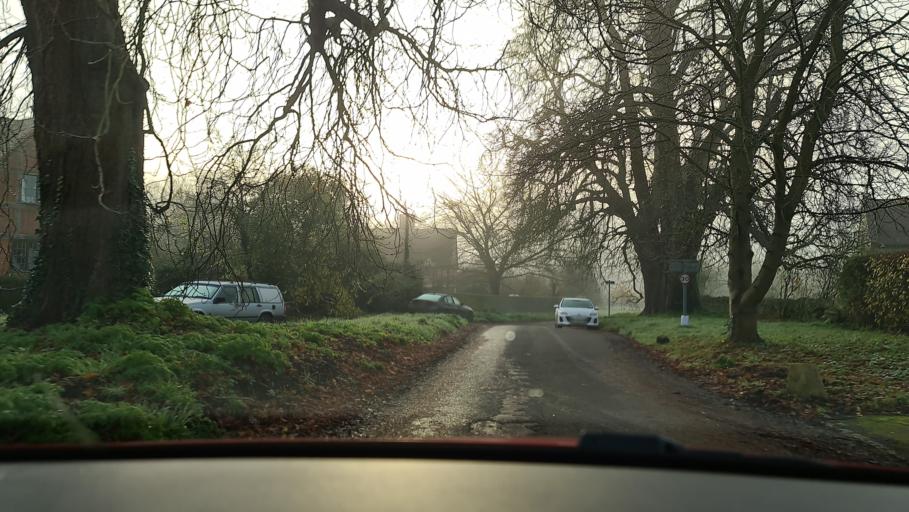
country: GB
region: England
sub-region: Buckinghamshire
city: Haddenham
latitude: 51.8048
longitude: -0.9387
